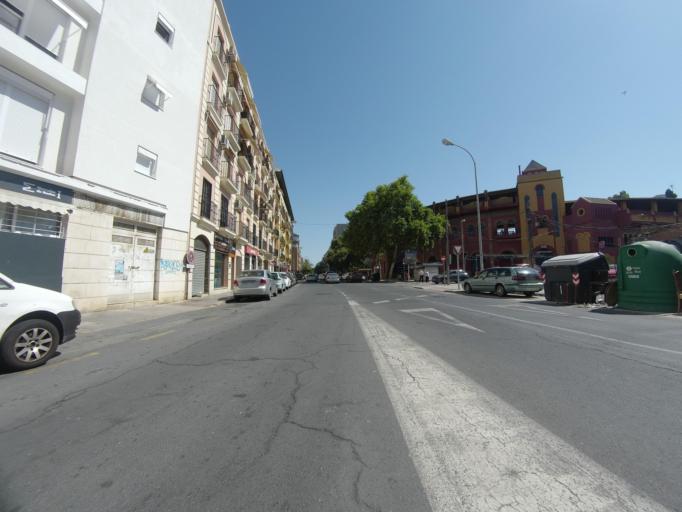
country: ES
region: Andalusia
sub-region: Provincia de Huelva
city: Huelva
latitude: 37.2649
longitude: -6.9525
